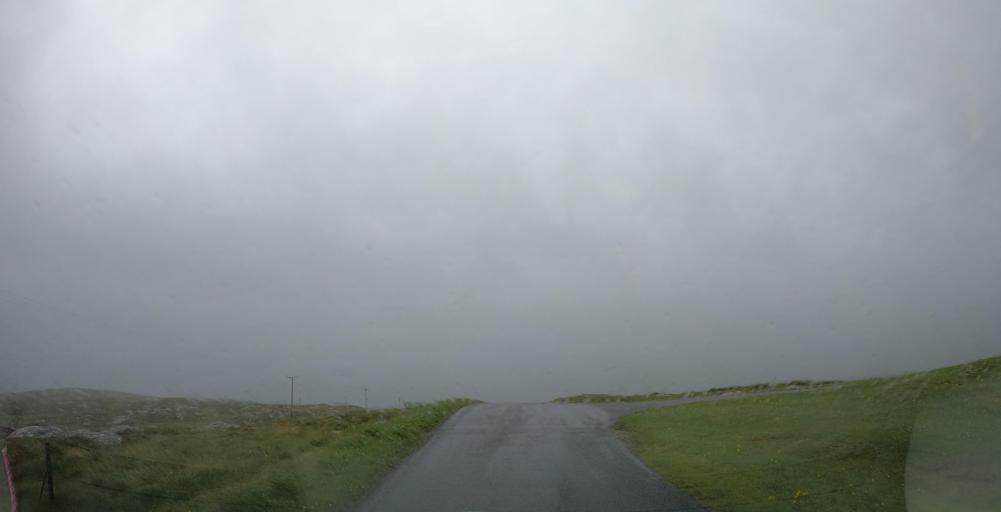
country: GB
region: Scotland
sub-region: Eilean Siar
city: Barra
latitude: 57.0107
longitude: -7.4247
